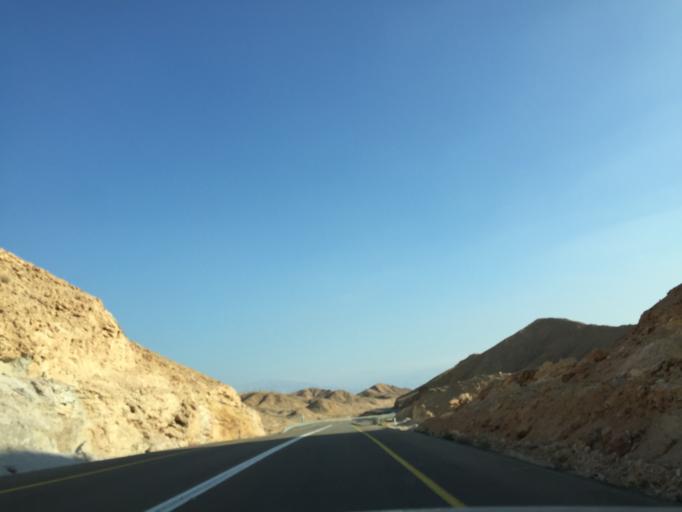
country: IL
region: Southern District
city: `En Boqeq
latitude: 31.1904
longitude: 35.2837
